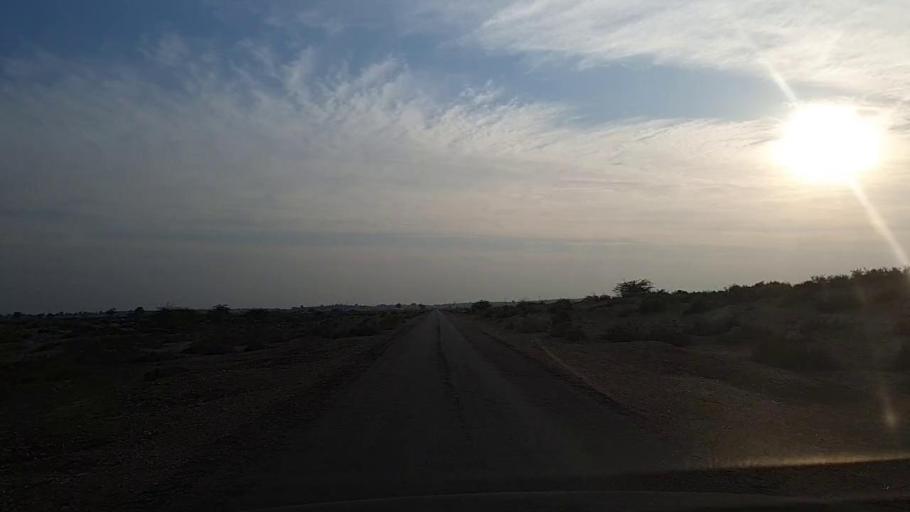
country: PK
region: Sindh
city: Jam Sahib
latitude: 26.4059
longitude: 68.5082
